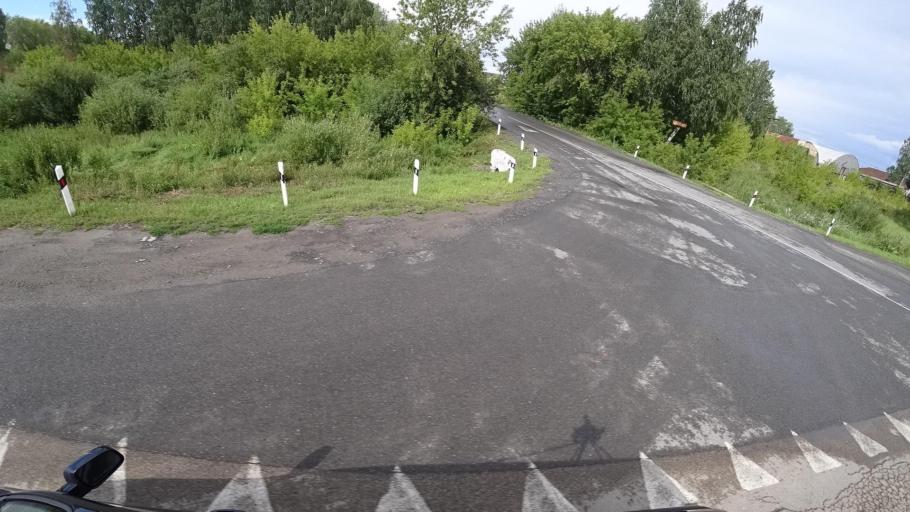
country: RU
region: Sverdlovsk
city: Kamyshlov
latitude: 56.8417
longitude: 62.7847
